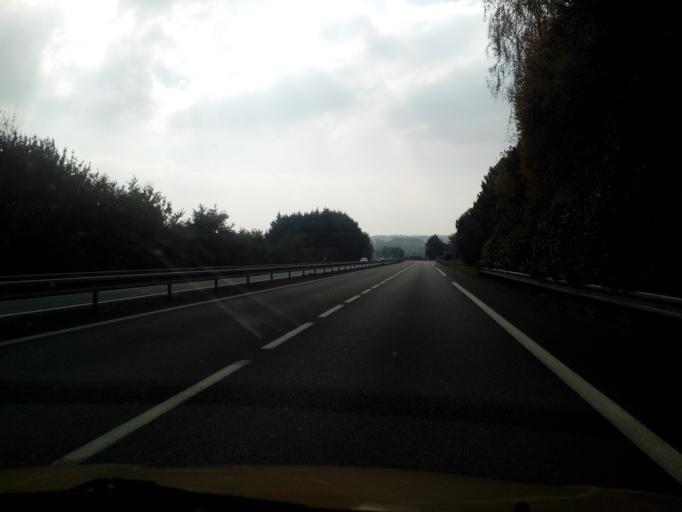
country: FR
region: Brittany
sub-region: Departement du Morbihan
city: Ploermel
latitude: 47.9020
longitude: -2.4117
